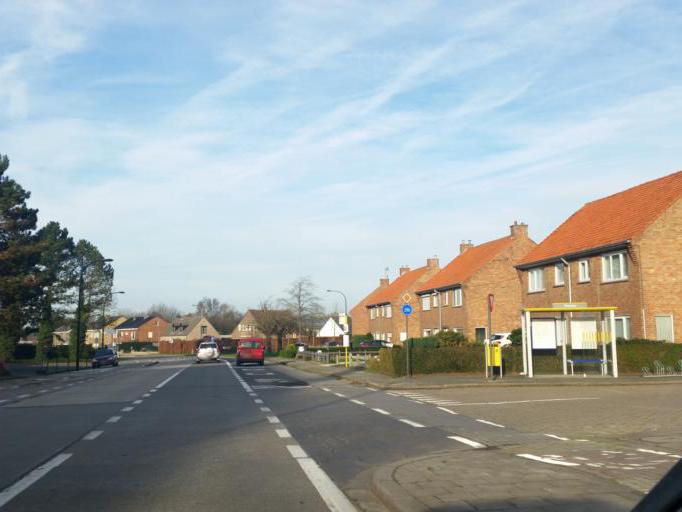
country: BE
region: Flanders
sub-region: Provincie Oost-Vlaanderen
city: Knesselare
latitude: 51.1432
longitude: 3.4068
